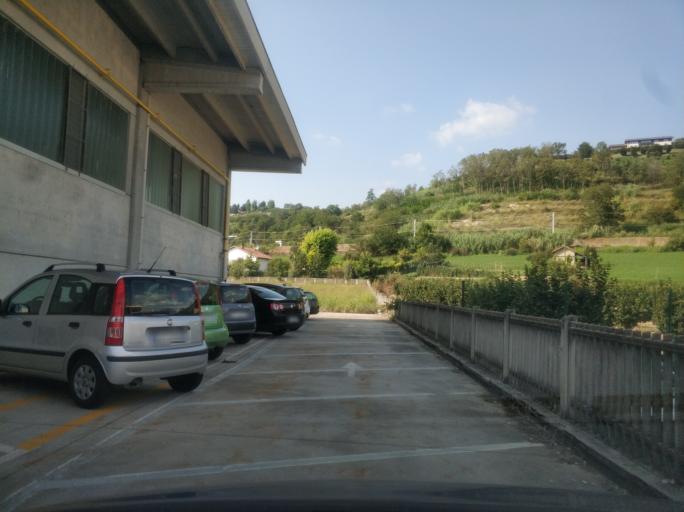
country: IT
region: Piedmont
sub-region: Provincia di Cuneo
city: Cinzano
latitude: 44.6957
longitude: 7.9087
